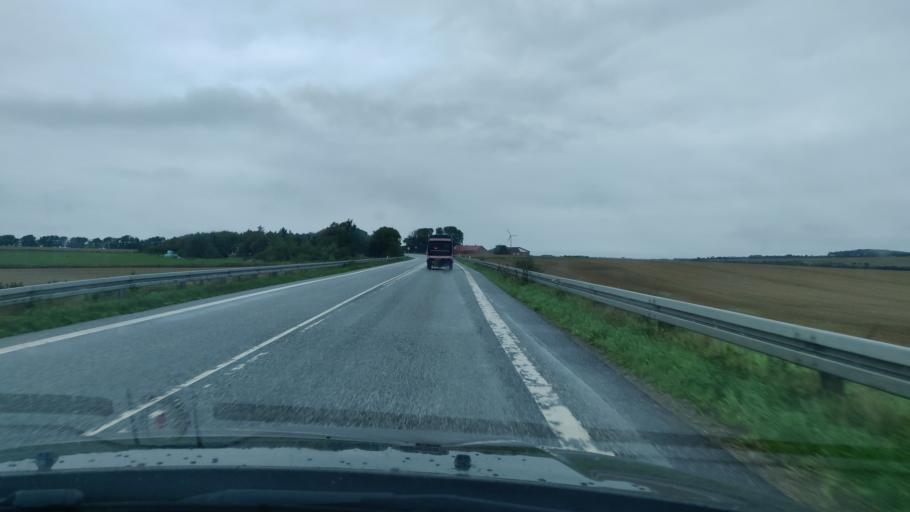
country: DK
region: North Denmark
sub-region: Thisted Kommune
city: Thisted
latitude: 56.9840
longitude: 8.7663
